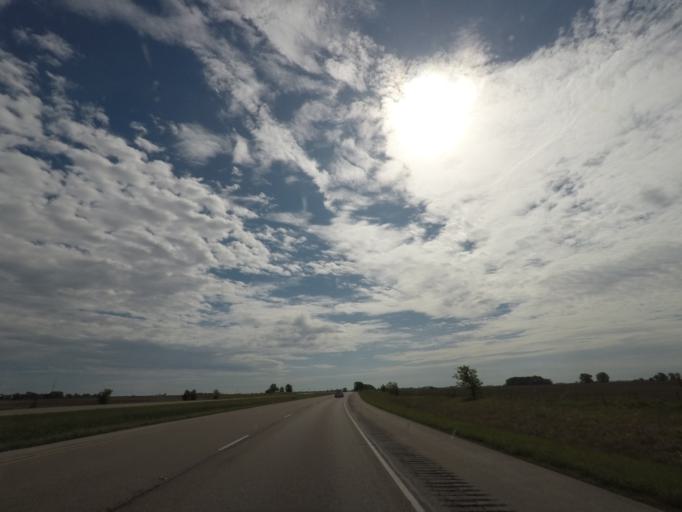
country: US
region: Illinois
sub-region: McLean County
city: Twin Grove
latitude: 40.3954
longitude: -89.0712
